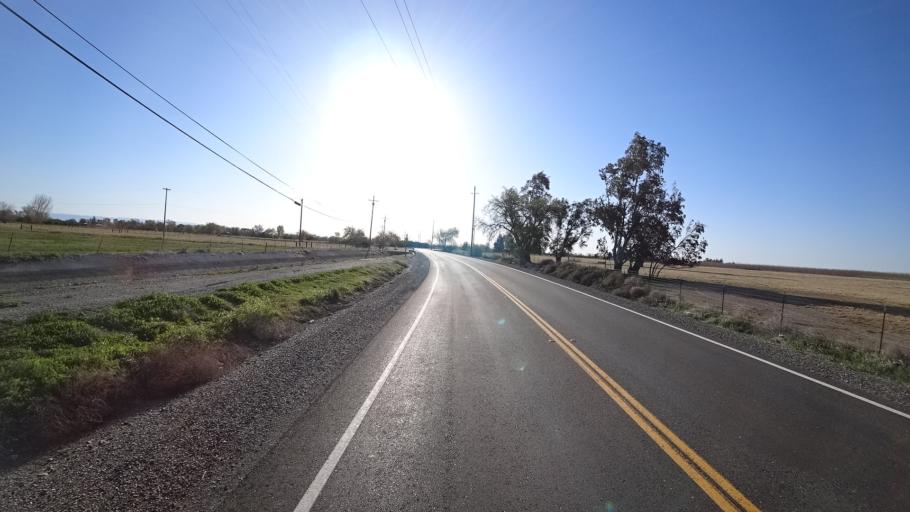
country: US
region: California
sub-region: Glenn County
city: Orland
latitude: 39.7701
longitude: -122.2580
